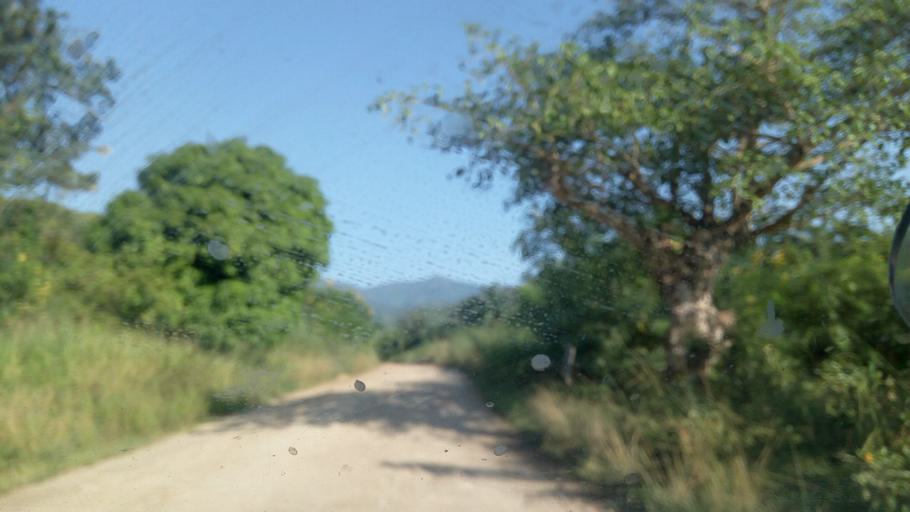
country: BI
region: Bururi
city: Rumonge
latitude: -4.0002
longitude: 29.0934
